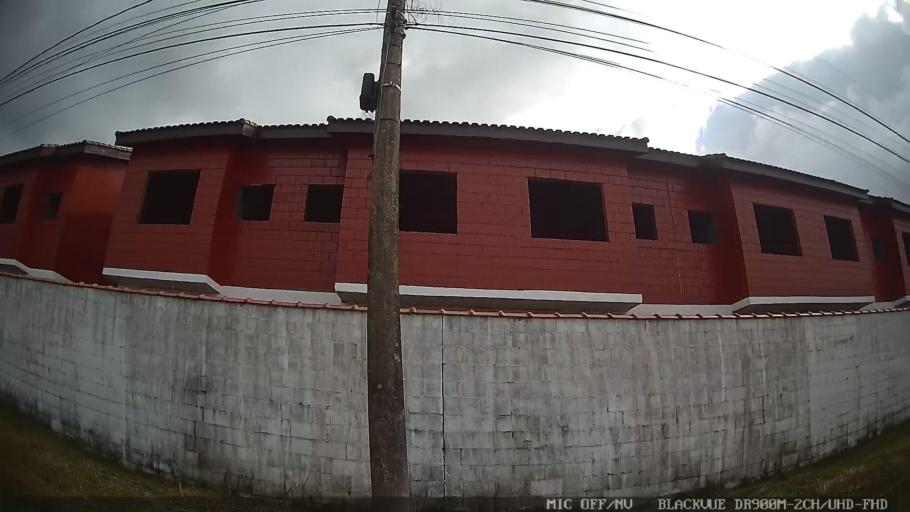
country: BR
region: Sao Paulo
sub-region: Itanhaem
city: Itanhaem
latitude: -24.1983
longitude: -46.8363
